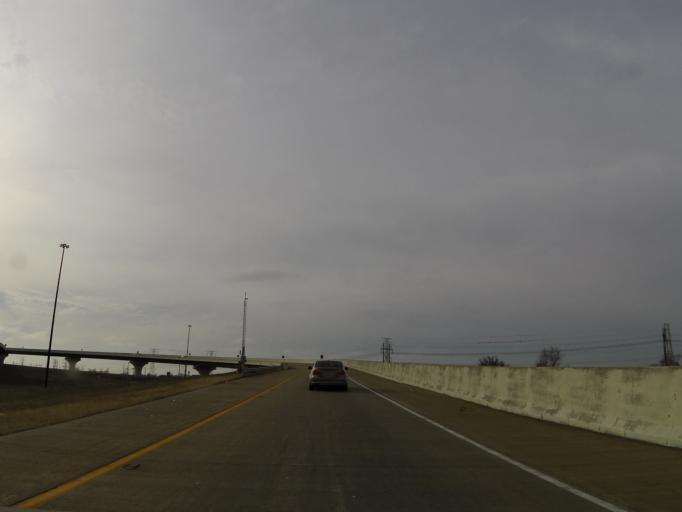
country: US
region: Indiana
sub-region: Marion County
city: Beech Grove
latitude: 39.7342
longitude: -86.0455
